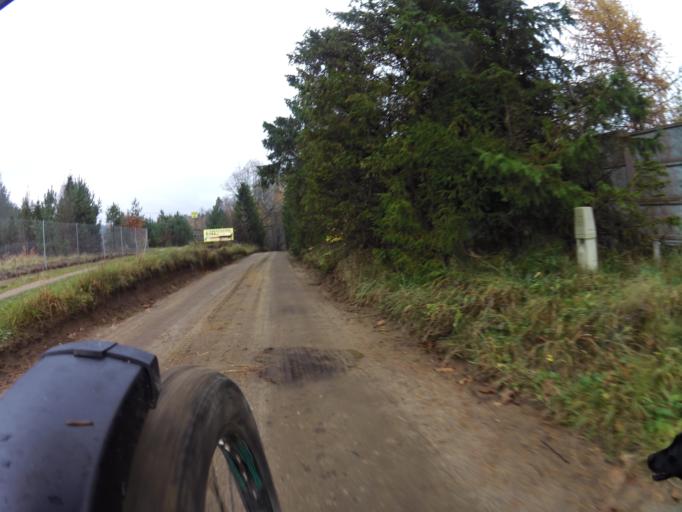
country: PL
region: Pomeranian Voivodeship
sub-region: Powiat wejherowski
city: Orle
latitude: 54.6895
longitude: 18.1518
